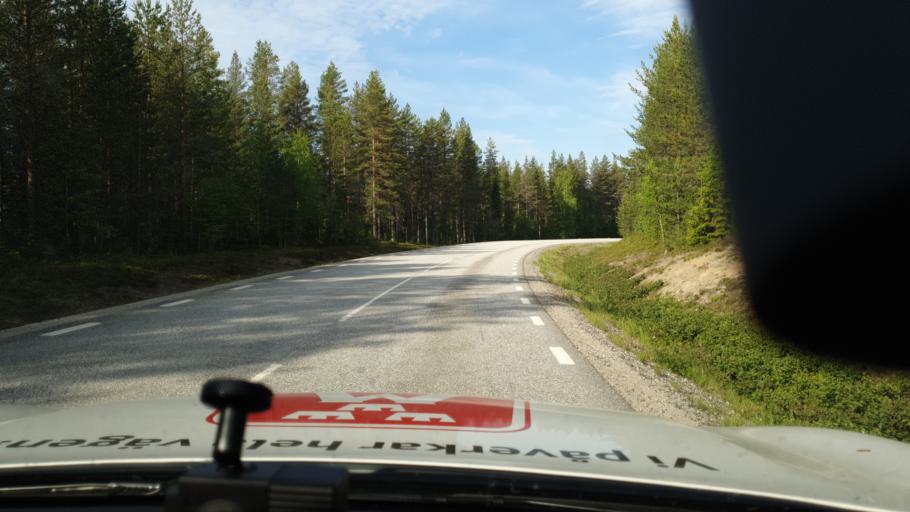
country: SE
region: Vaesterbotten
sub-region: Vindelns Kommun
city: Vindeln
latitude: 64.2039
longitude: 19.4802
